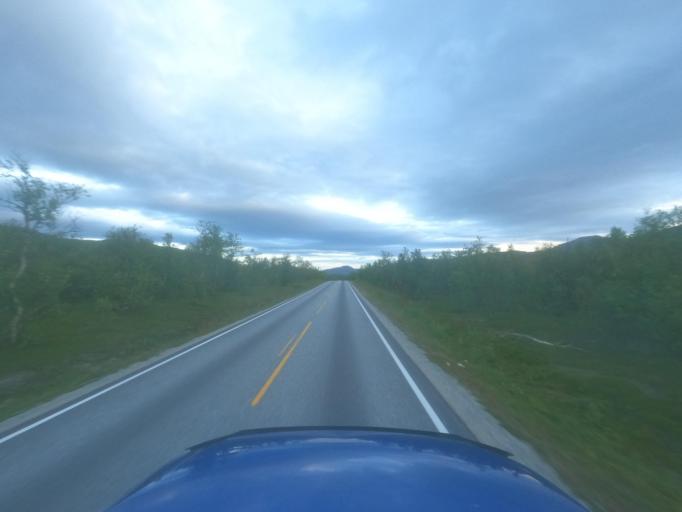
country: NO
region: Finnmark Fylke
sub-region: Porsanger
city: Lakselv
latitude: 69.9479
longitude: 24.9580
